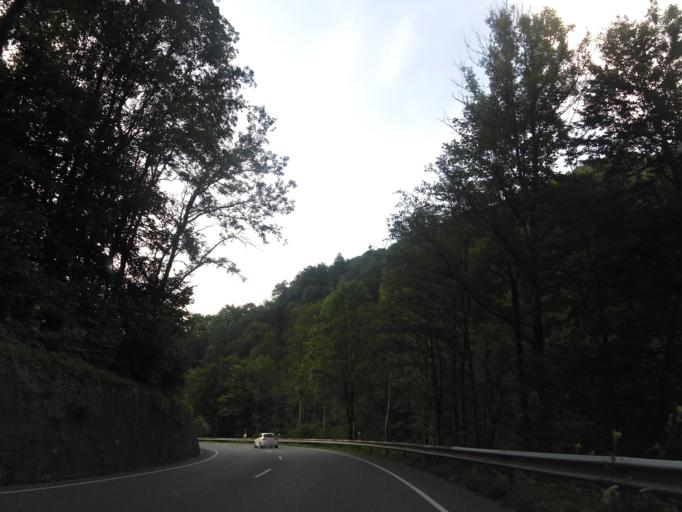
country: DE
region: Bavaria
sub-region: Upper Bavaria
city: Marktschellenberg
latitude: 47.6998
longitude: 13.0432
